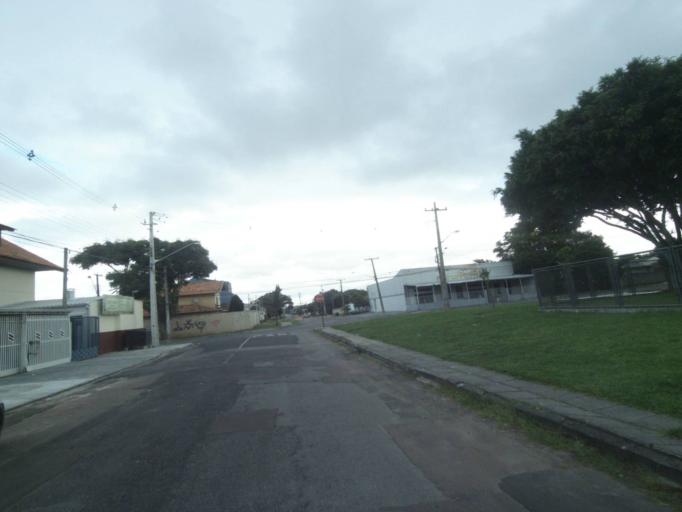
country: BR
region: Parana
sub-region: Pinhais
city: Pinhais
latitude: -25.4568
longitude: -49.2068
